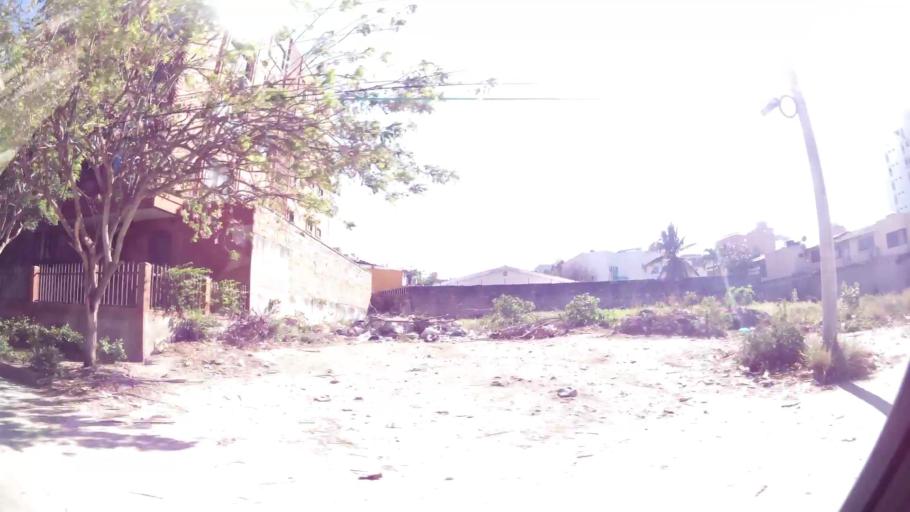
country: CO
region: Atlantico
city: Barranquilla
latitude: 11.0185
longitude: -74.8186
